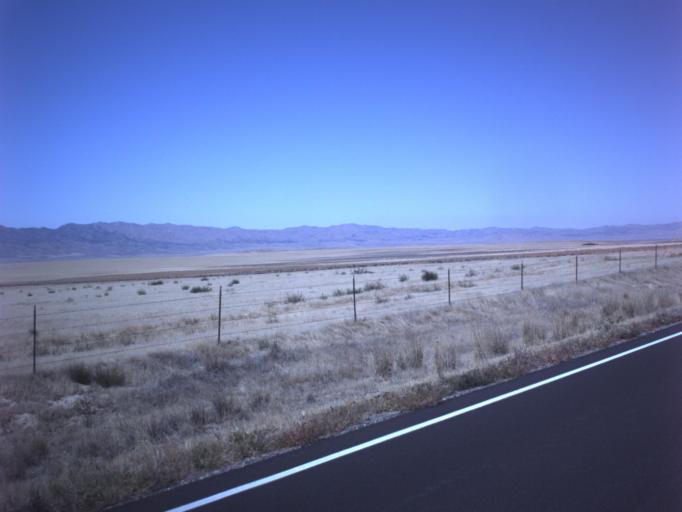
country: US
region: Utah
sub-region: Tooele County
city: Grantsville
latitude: 40.4159
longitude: -112.7487
